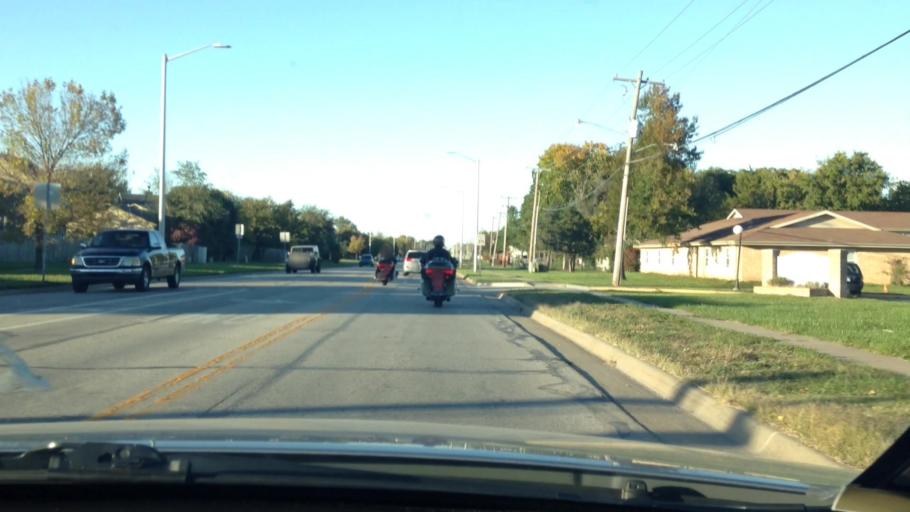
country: US
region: Kansas
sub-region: Johnson County
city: Gardner
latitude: 38.8167
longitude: -94.9276
